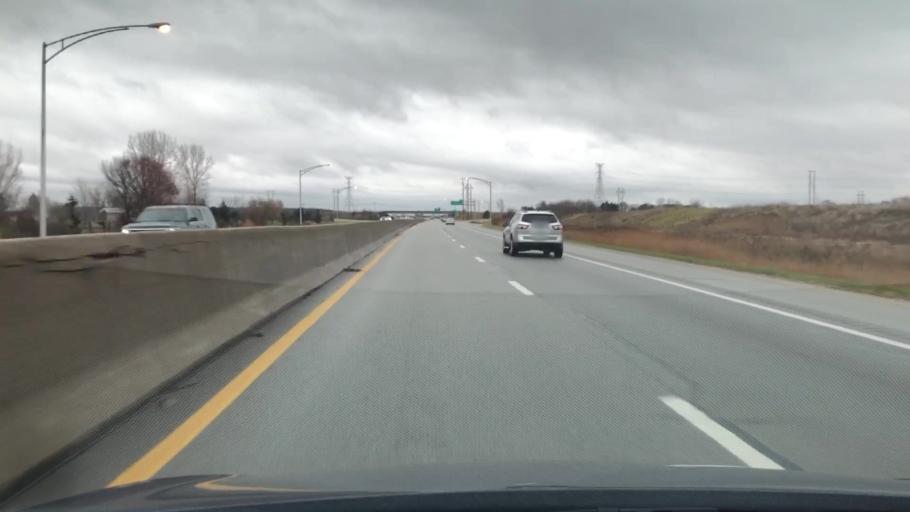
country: US
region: Ohio
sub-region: Wood County
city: Northwood
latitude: 41.5942
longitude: -83.4769
